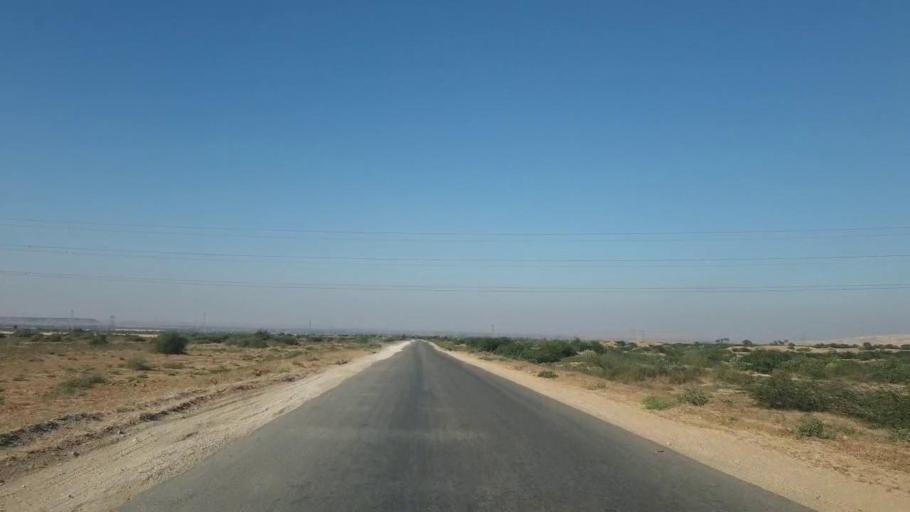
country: PK
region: Sindh
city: Gharo
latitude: 25.1619
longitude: 67.6630
